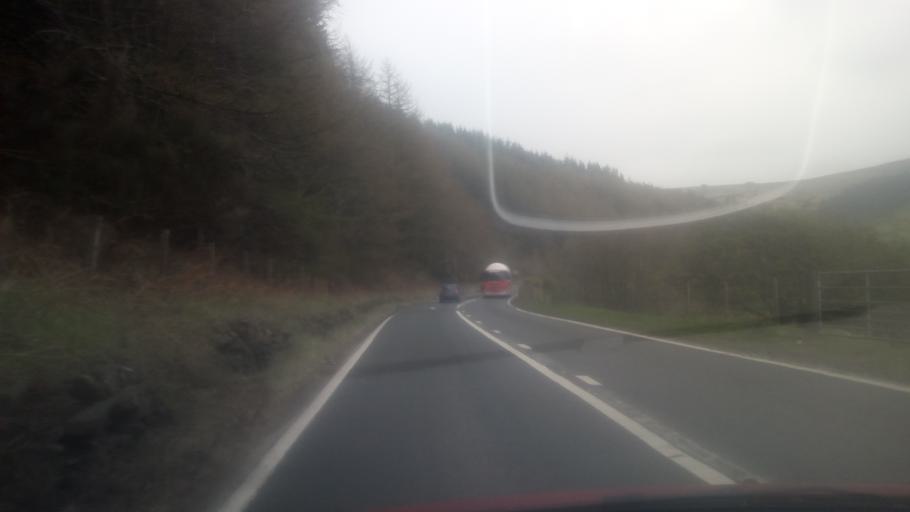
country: GB
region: Scotland
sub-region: The Scottish Borders
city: Galashiels
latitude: 55.7079
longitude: -2.8862
